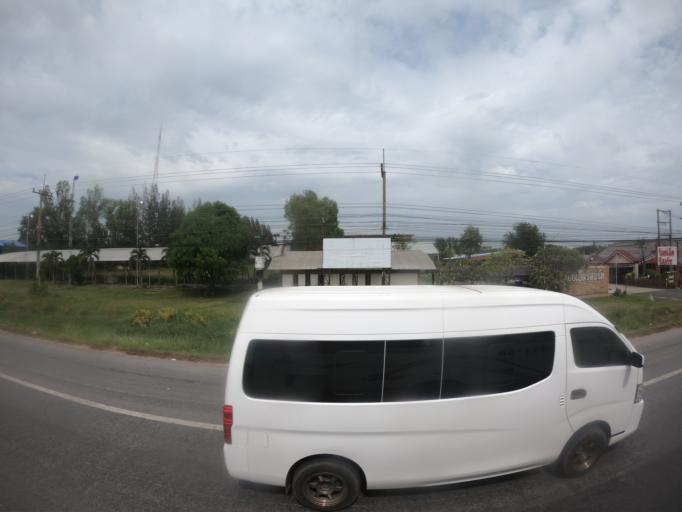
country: TH
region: Roi Et
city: Roi Et
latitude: 16.0720
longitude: 103.5982
